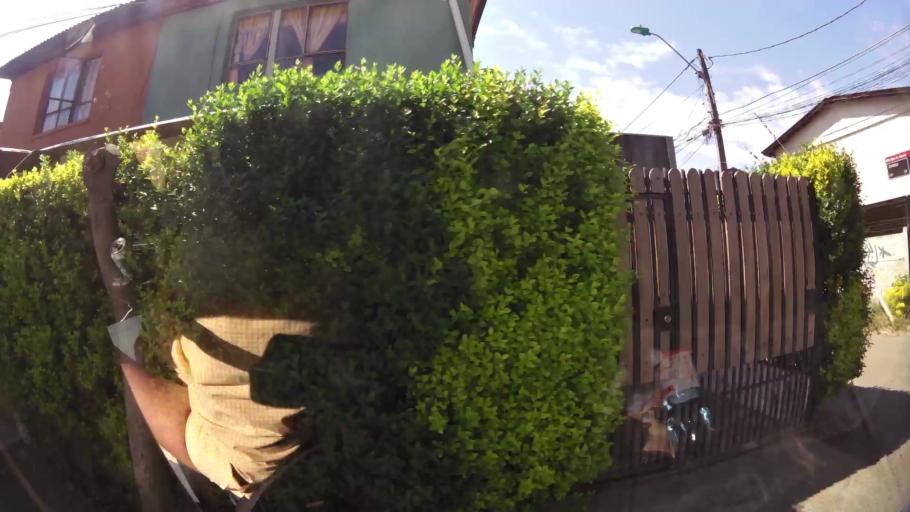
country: CL
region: Santiago Metropolitan
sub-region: Provincia de Talagante
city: Talagante
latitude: -33.6561
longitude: -70.9162
